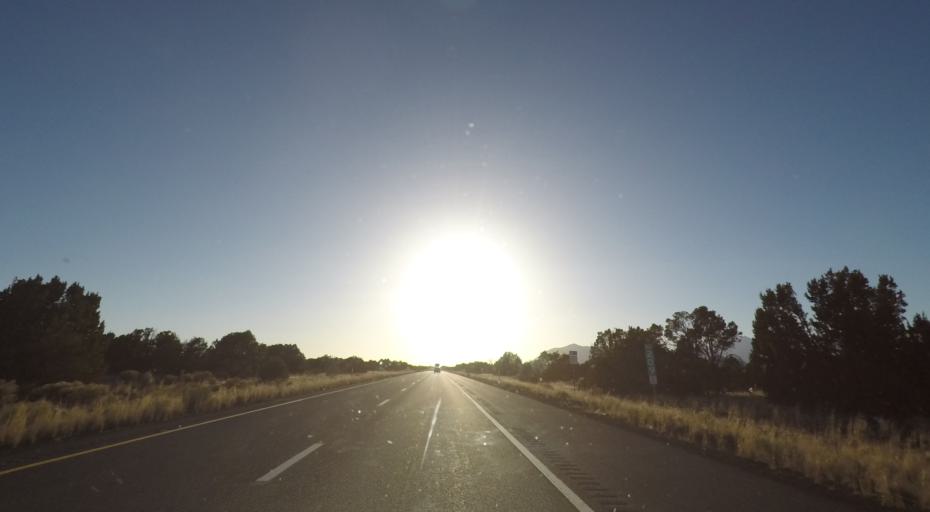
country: US
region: Arizona
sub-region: Coconino County
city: Flagstaff
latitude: 35.2023
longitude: -111.4446
